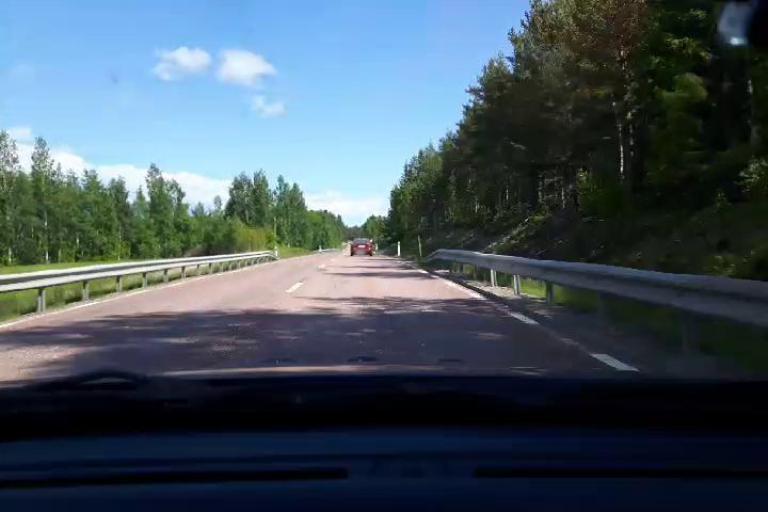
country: SE
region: Gaevleborg
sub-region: Hudiksvalls Kommun
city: Delsbo
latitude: 61.7973
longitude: 16.5089
